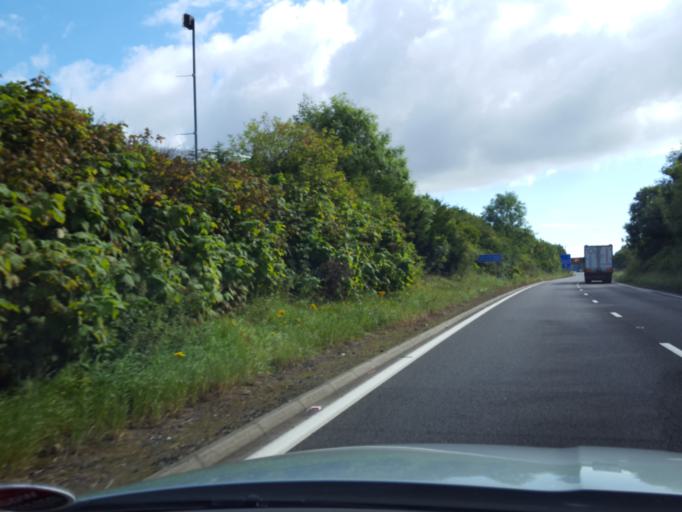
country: GB
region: Scotland
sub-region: Fife
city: Rosyth
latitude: 56.0472
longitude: -3.4246
